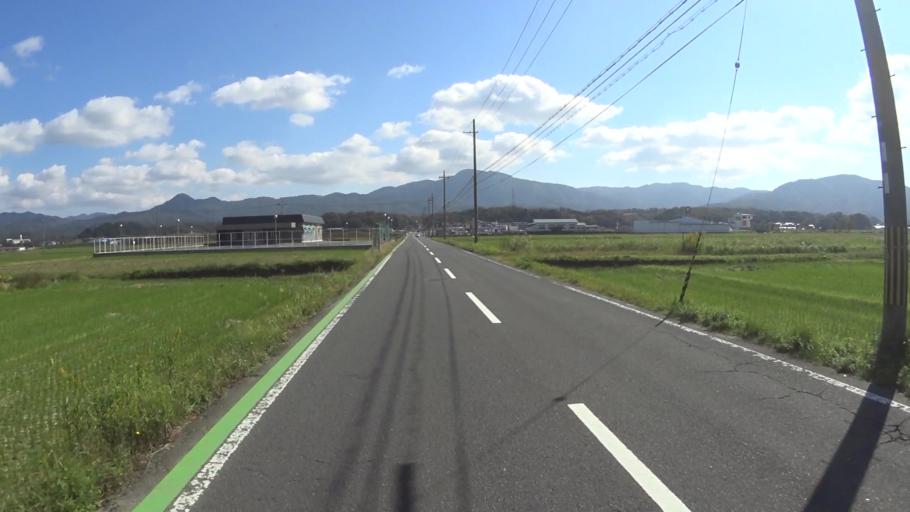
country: JP
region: Kyoto
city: Miyazu
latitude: 35.6704
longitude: 135.0829
